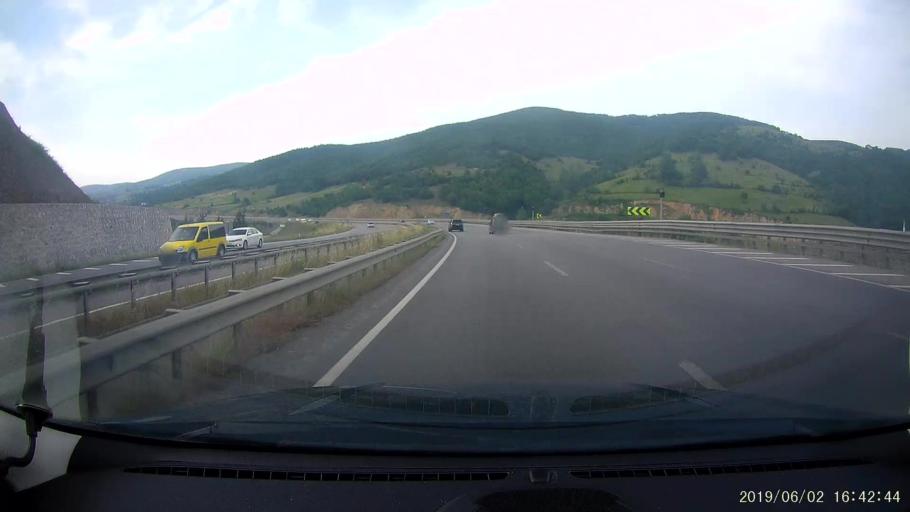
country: TR
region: Samsun
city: Kavak
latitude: 41.1226
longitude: 36.1377
